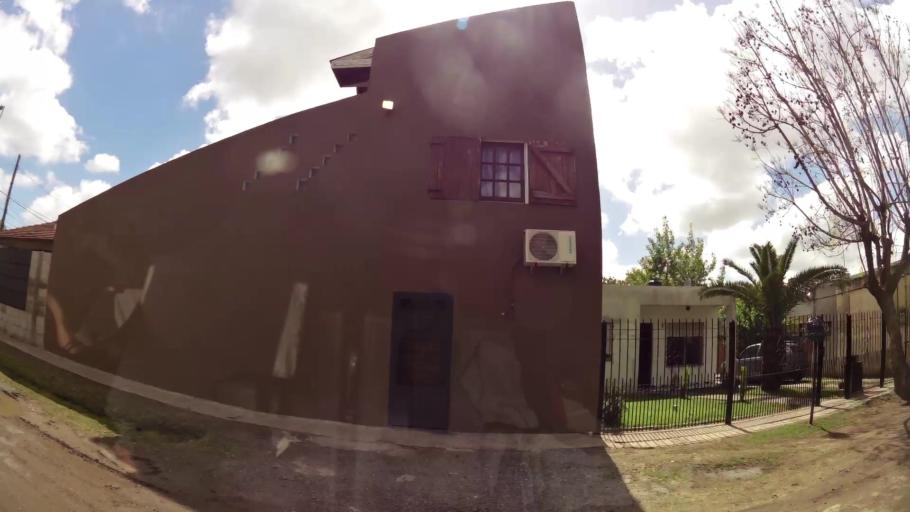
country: AR
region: Buenos Aires
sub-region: Partido de Quilmes
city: Quilmes
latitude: -34.8280
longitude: -58.2143
